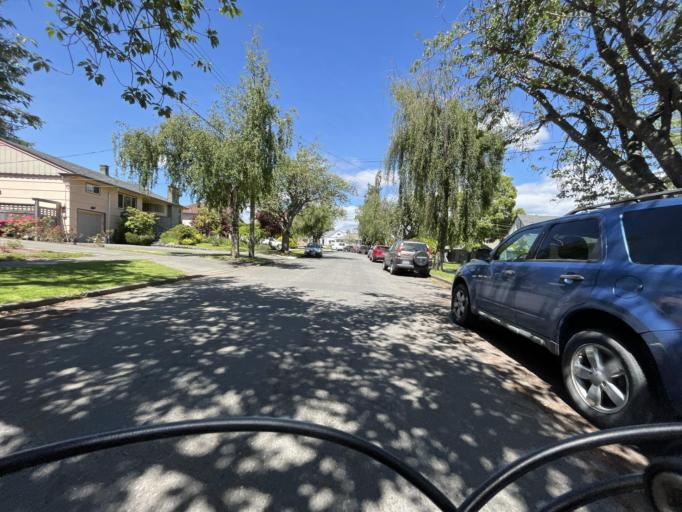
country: CA
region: British Columbia
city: Victoria
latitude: 48.4403
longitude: -123.3904
